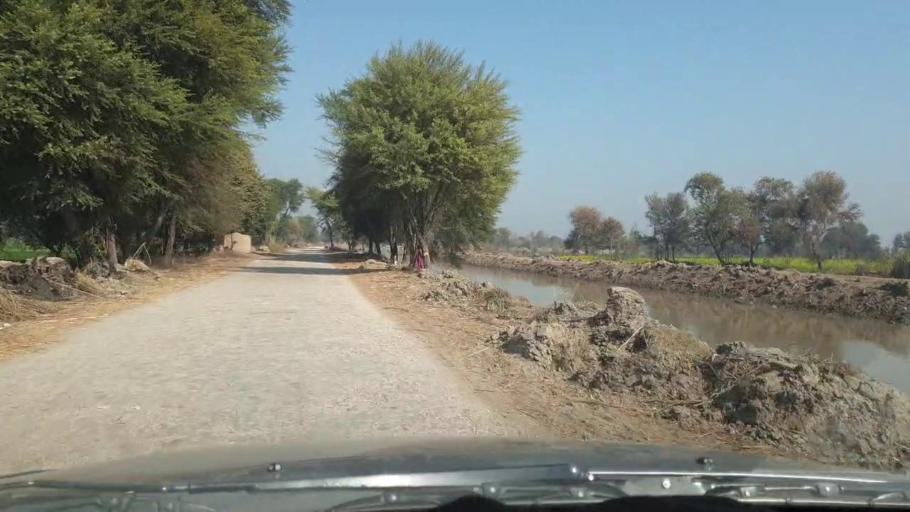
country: PK
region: Sindh
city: Khanpur
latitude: 27.7732
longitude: 69.5357
